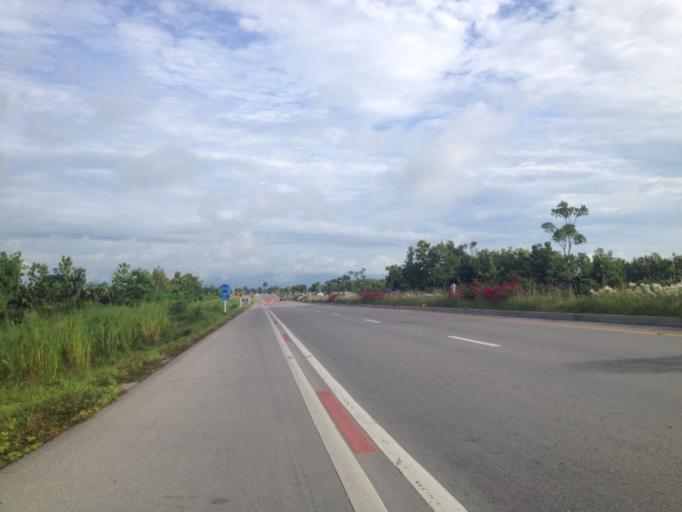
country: TH
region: Chiang Mai
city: San Pa Tong
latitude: 18.5591
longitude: 98.8496
